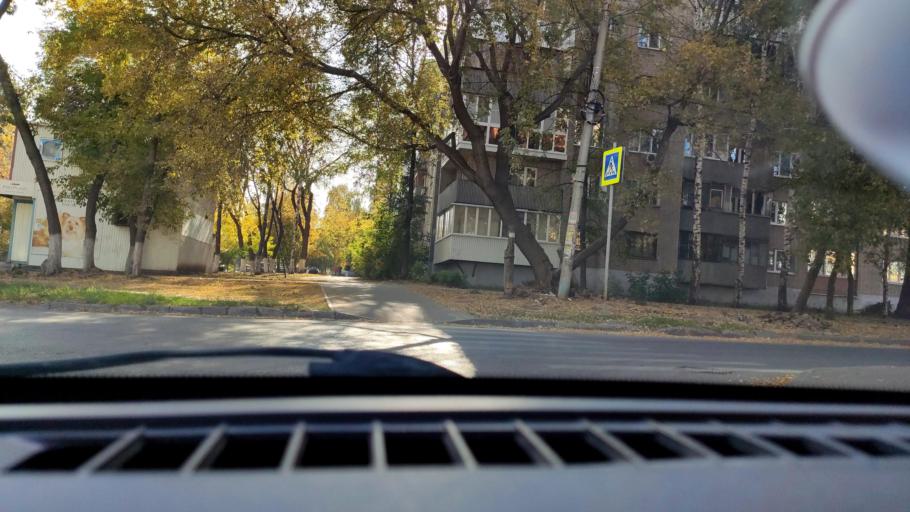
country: RU
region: Samara
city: Samara
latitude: 53.2134
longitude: 50.1680
